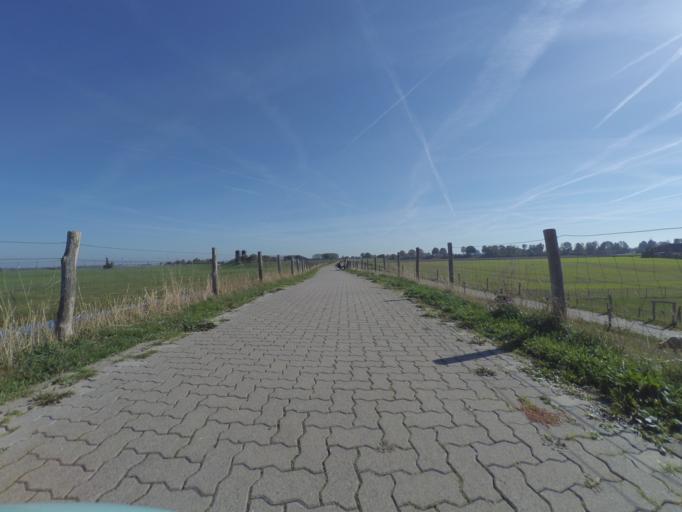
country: DE
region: North Rhine-Westphalia
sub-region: Regierungsbezirk Dusseldorf
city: Kleve
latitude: 51.8237
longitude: 6.1702
